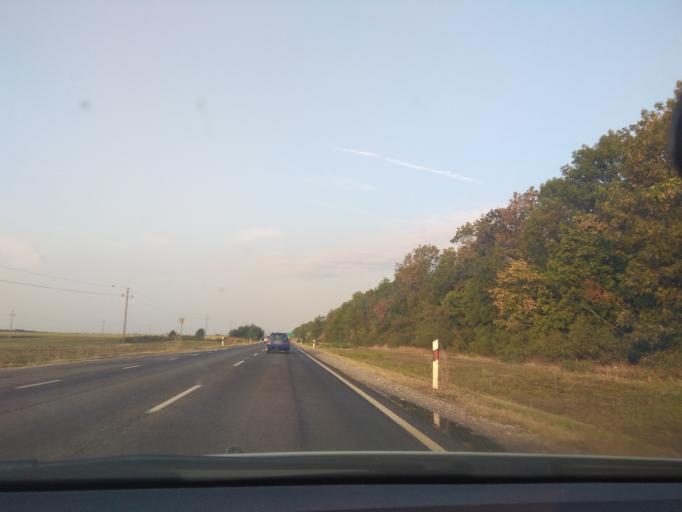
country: HU
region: Borsod-Abauj-Zemplen
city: Mezokovesd
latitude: 47.8277
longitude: 20.6130
